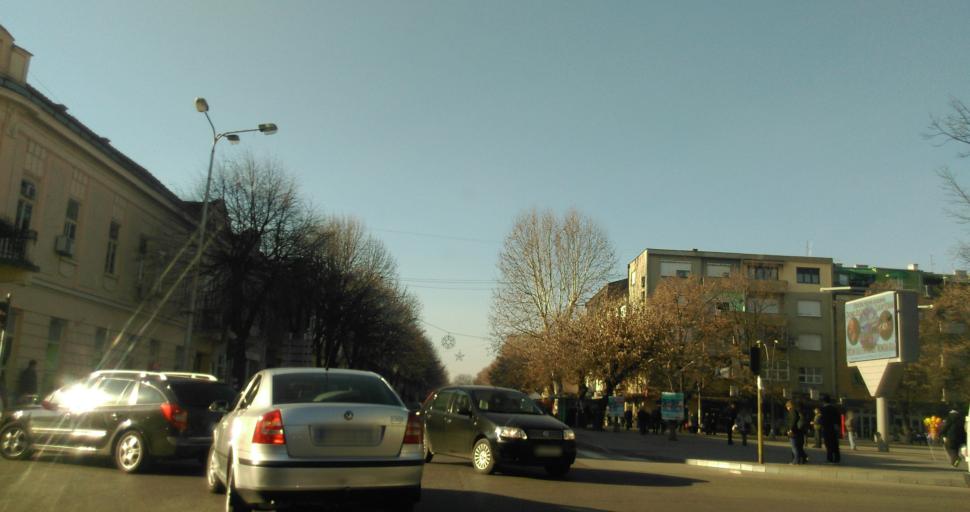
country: RS
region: Autonomna Pokrajina Vojvodina
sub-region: Sremski Okrug
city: Ruma
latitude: 45.0080
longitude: 19.8228
